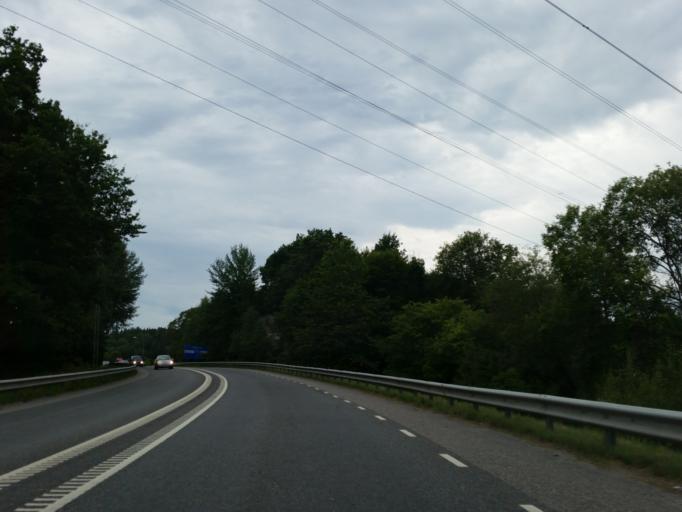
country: SE
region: Stockholm
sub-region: Botkyrka Kommun
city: Tumba
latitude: 59.2177
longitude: 17.8301
